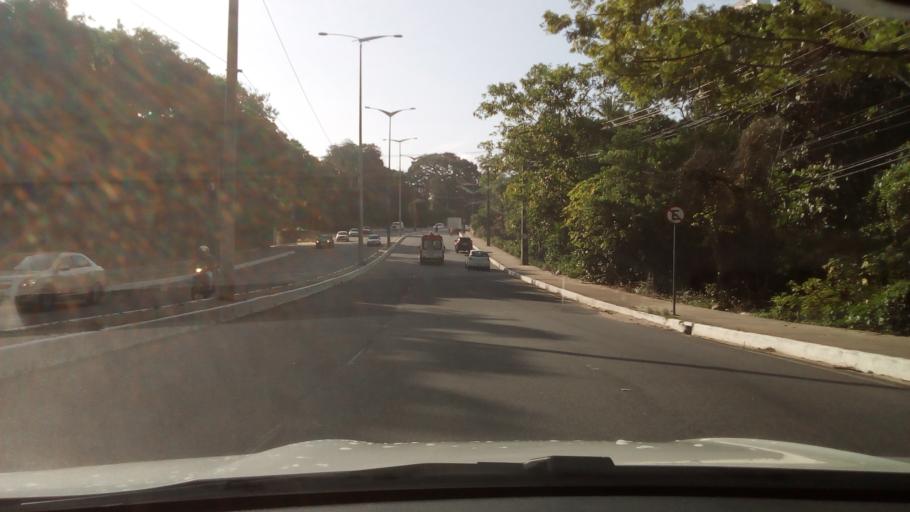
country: BR
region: Paraiba
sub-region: Joao Pessoa
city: Joao Pessoa
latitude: -7.1354
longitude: -34.8581
